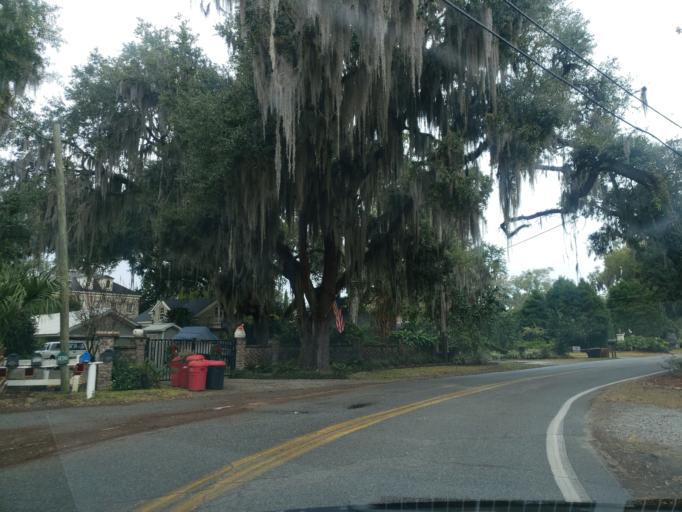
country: US
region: Georgia
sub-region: Chatham County
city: Wilmington Island
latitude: 31.9749
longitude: -81.0009
